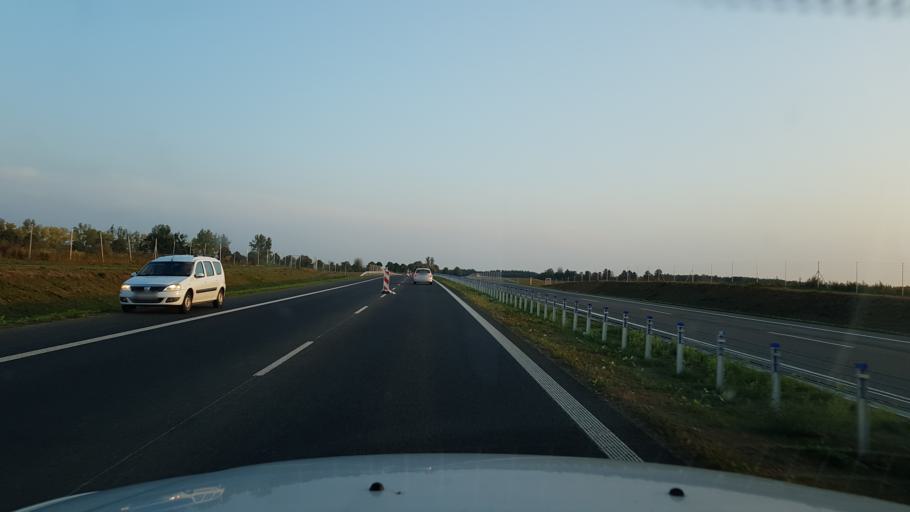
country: PL
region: West Pomeranian Voivodeship
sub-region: Powiat gryficki
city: Ploty
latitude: 53.7709
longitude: 15.2369
